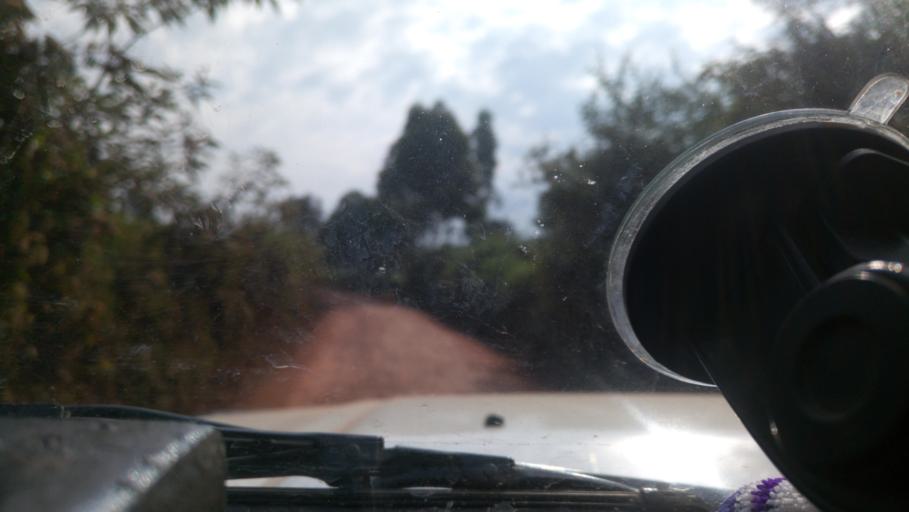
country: KE
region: Kericho
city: Litein
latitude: -0.5619
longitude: 35.1927
